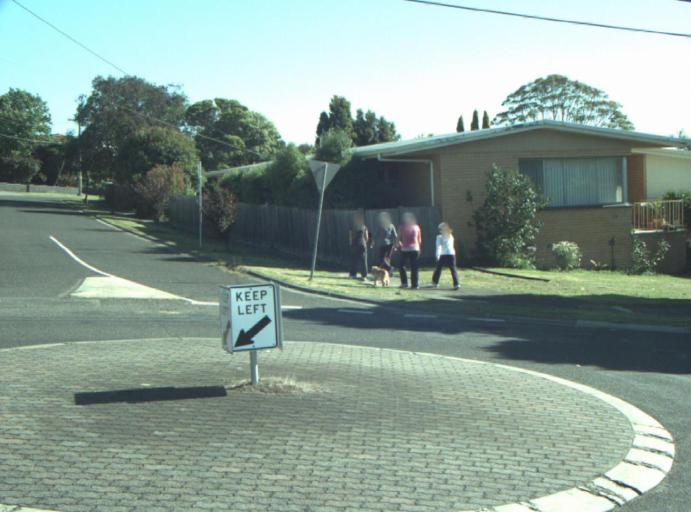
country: AU
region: Victoria
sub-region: Greater Geelong
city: Hamlyn Heights
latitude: -38.1163
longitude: 144.3266
